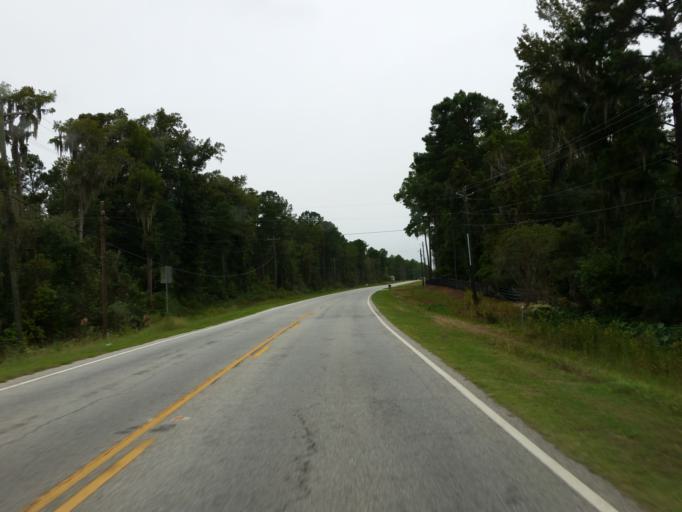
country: US
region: Georgia
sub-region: Lanier County
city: Lakeland
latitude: 31.0422
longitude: -83.0941
